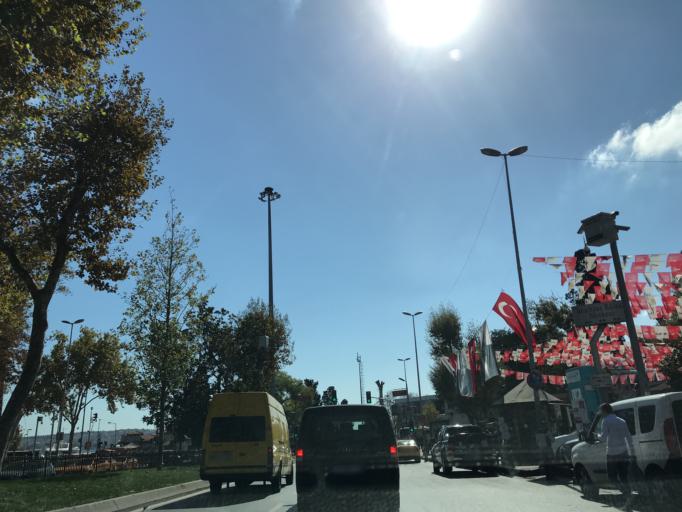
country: TR
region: Istanbul
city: Sisli
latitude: 41.0432
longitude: 29.0069
